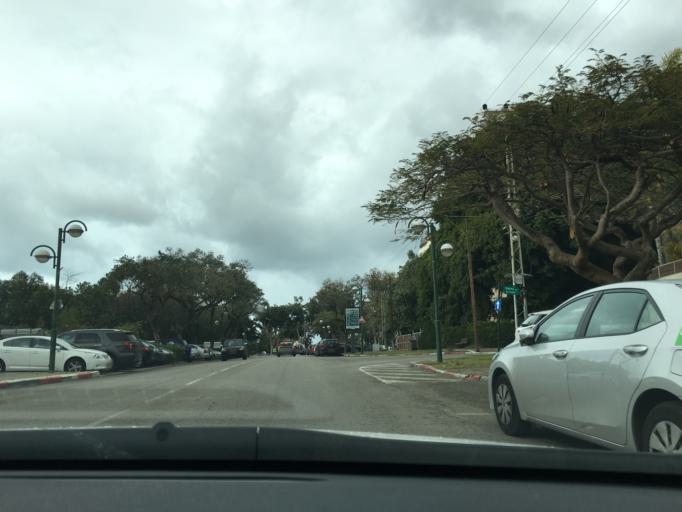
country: IL
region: Tel Aviv
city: Ramat HaSharon
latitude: 32.1437
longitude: 34.8457
